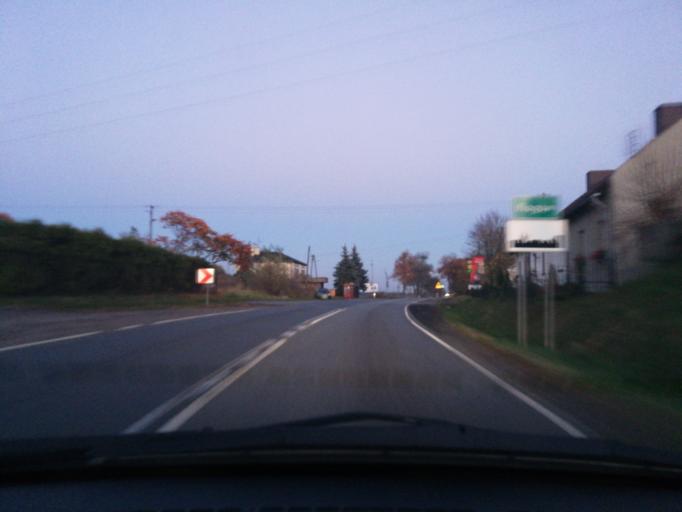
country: PL
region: Lodz Voivodeship
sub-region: Powiat brzezinski
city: Rogow
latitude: 51.8074
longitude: 19.8509
